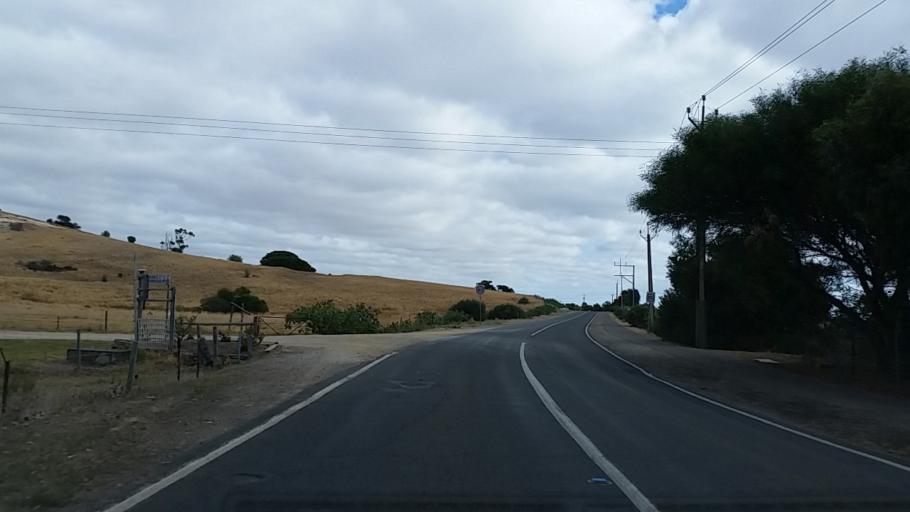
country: AU
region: South Australia
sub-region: Yankalilla
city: Normanville
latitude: -35.4319
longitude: 138.3245
